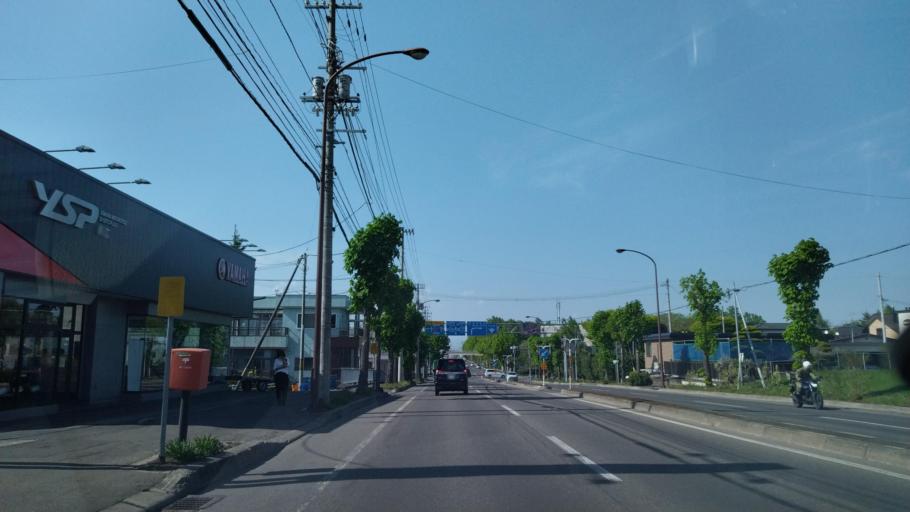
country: JP
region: Hokkaido
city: Obihiro
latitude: 42.8961
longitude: 143.1814
